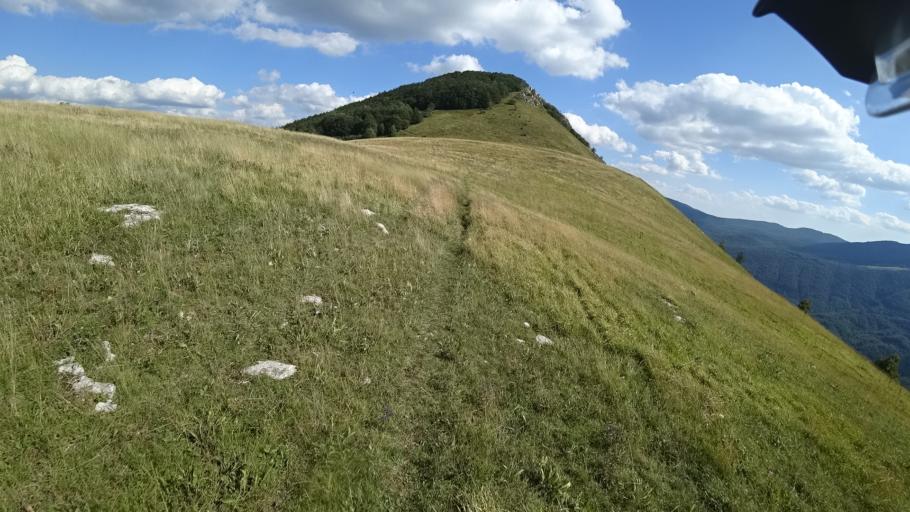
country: HR
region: Zadarska
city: Gracac
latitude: 44.3848
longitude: 16.0451
